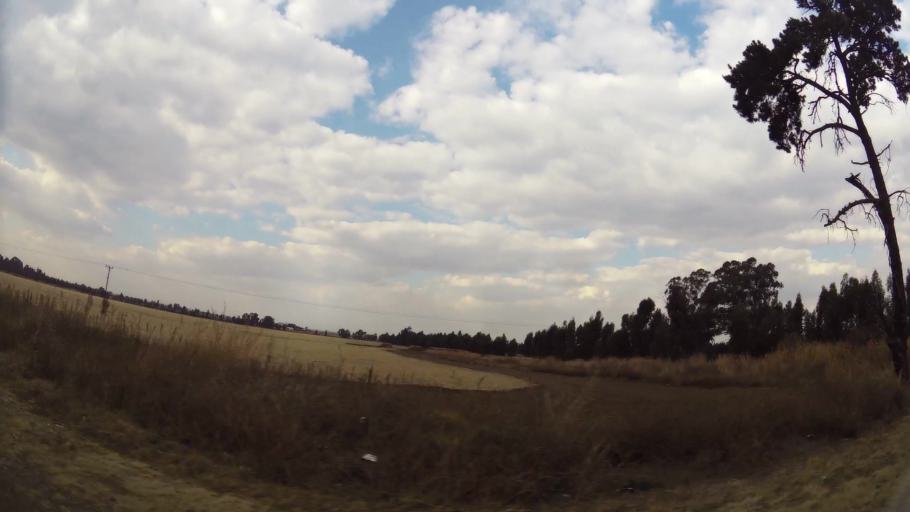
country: ZA
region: Mpumalanga
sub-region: Nkangala District Municipality
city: Delmas
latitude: -26.2432
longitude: 28.6328
